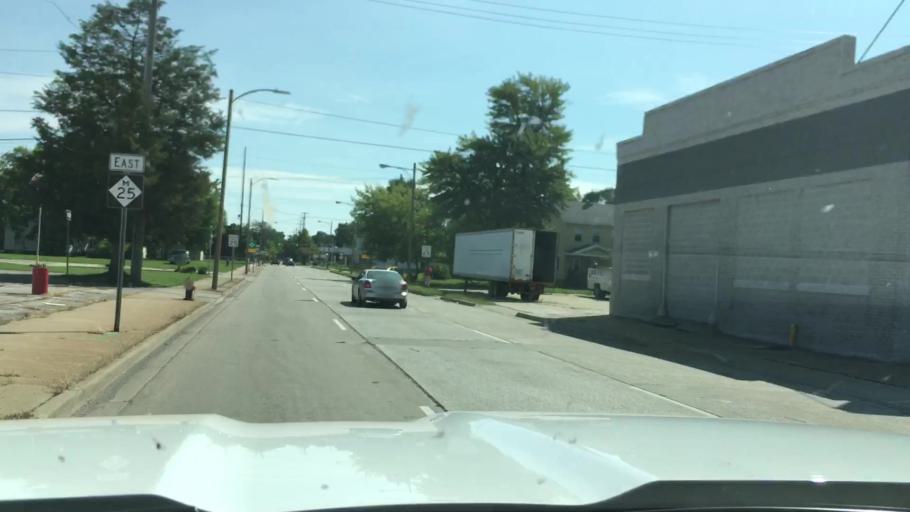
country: US
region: Michigan
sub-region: Bay County
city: Bay City
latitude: 43.5950
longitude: -83.8880
